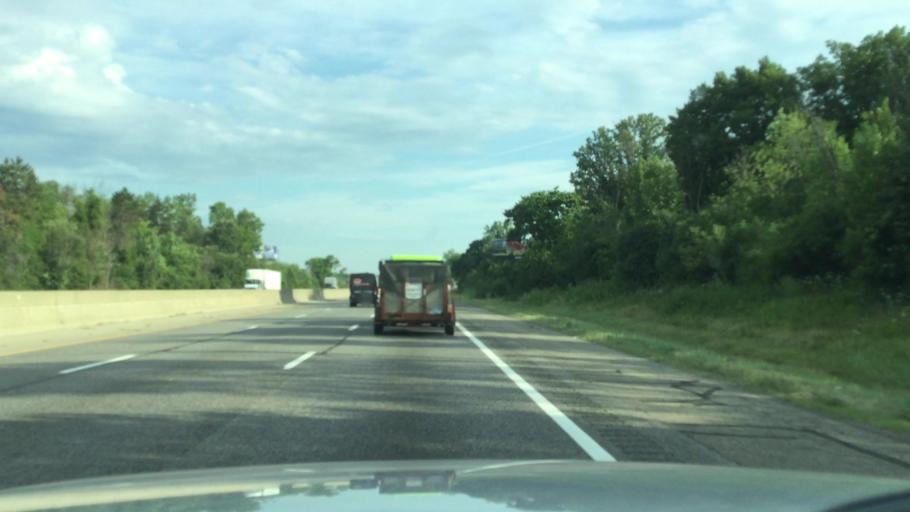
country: US
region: Michigan
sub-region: Genesee County
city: Beecher
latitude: 43.0515
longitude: -83.7581
